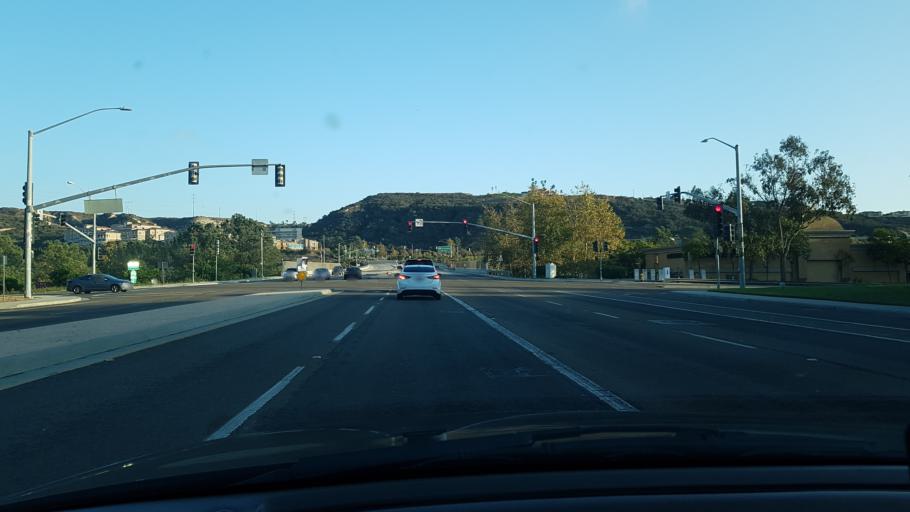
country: US
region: California
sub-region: San Diego County
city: Del Mar
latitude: 32.9387
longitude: -117.2300
